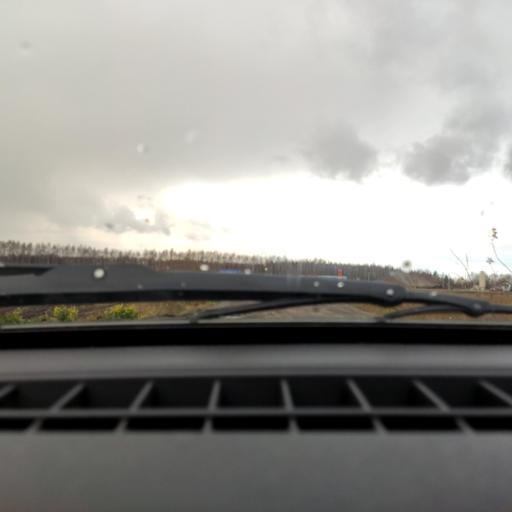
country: RU
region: Bashkortostan
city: Iglino
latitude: 54.7442
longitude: 56.3154
